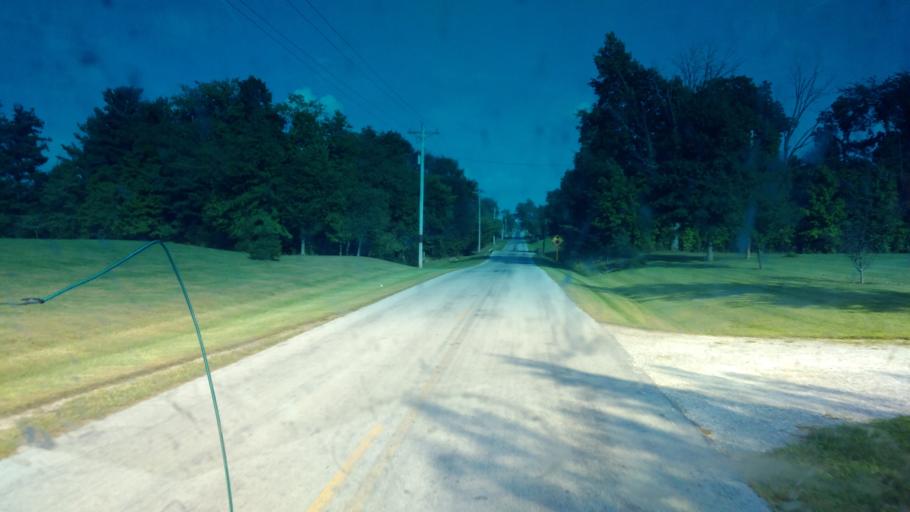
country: US
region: Ohio
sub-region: Wyandot County
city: Carey
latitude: 40.9052
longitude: -83.3843
